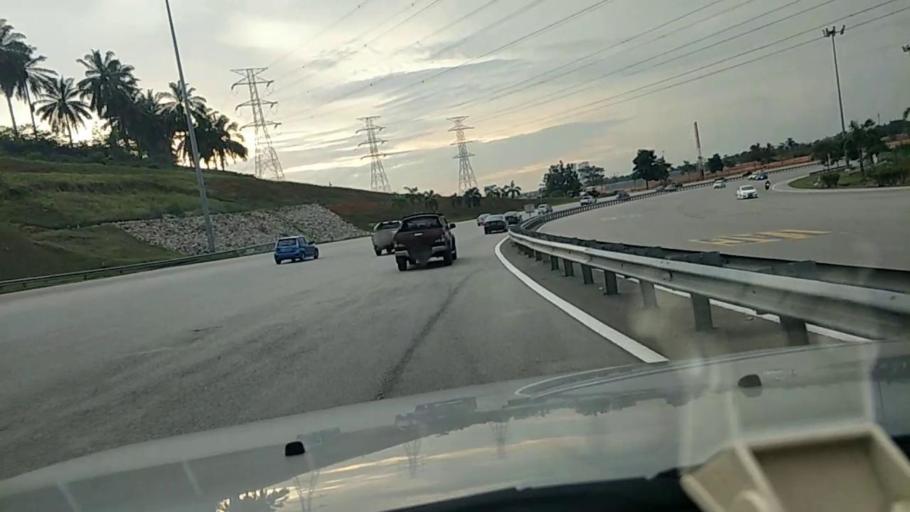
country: MY
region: Selangor
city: Shah Alam
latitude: 3.0920
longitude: 101.4837
